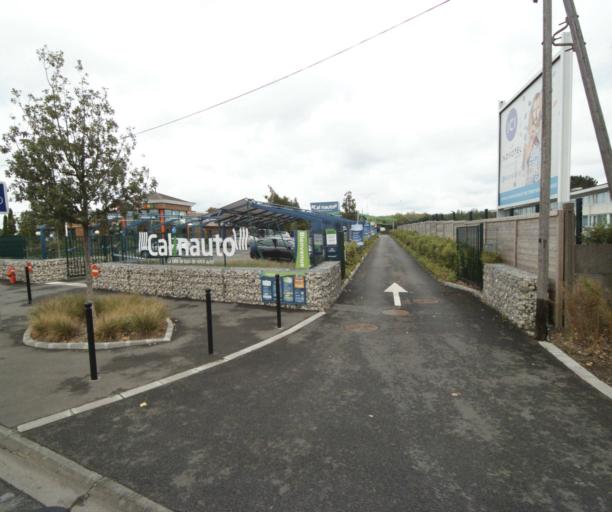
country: FR
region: Nord-Pas-de-Calais
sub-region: Departement du Nord
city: Vendeville
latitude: 50.5843
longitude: 3.0883
